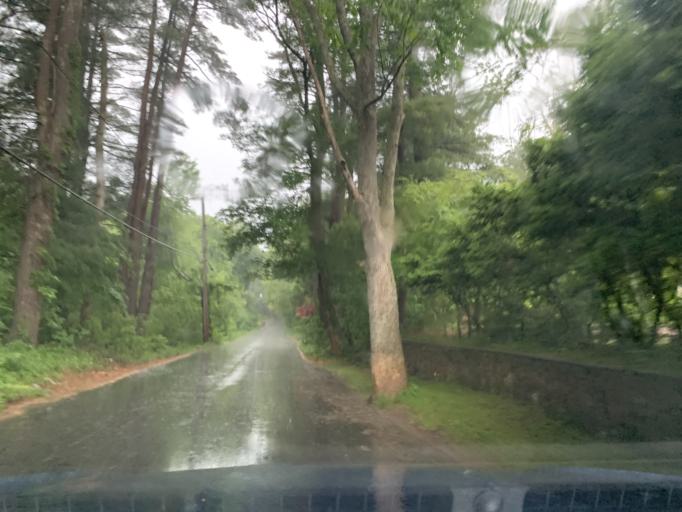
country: US
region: Rhode Island
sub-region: Kent County
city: West Warwick
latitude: 41.7289
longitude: -71.5526
